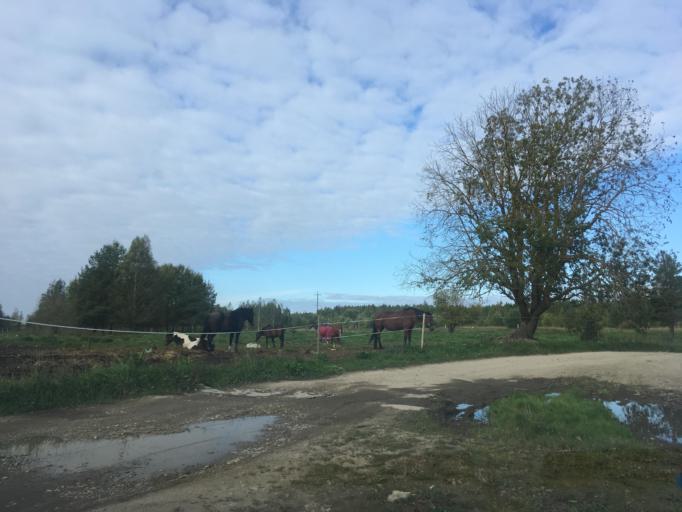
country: EE
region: Harju
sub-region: Maardu linn
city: Maardu
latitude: 59.4528
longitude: 25.0484
